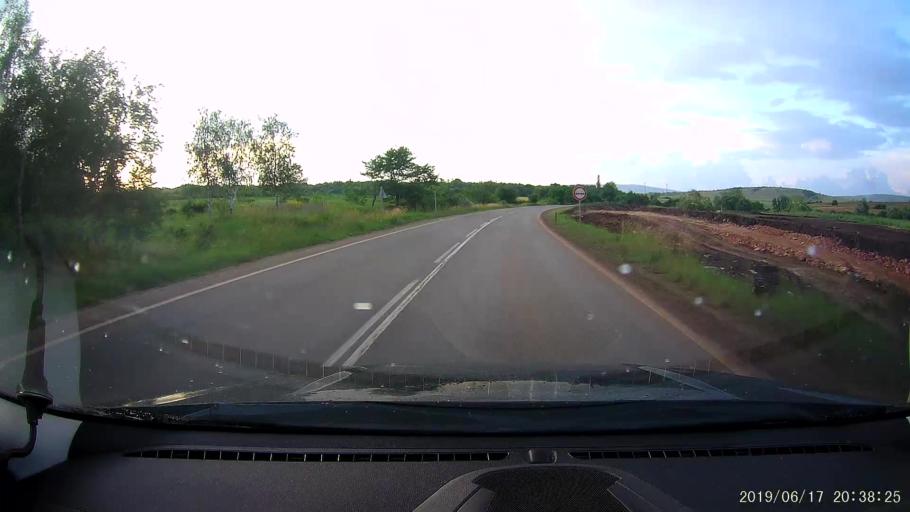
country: BG
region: Sofiya
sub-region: Obshtina Slivnitsa
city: Slivnitsa
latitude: 42.8718
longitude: 23.0185
